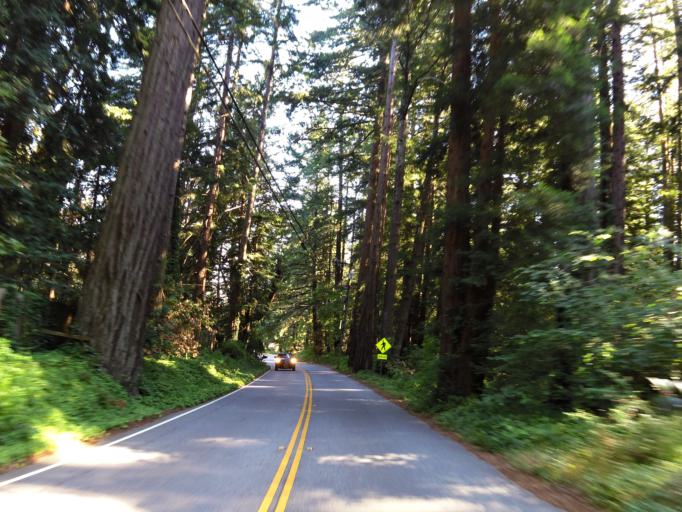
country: US
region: California
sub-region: Santa Cruz County
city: Bonny Doon
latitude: 37.0432
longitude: -122.1503
